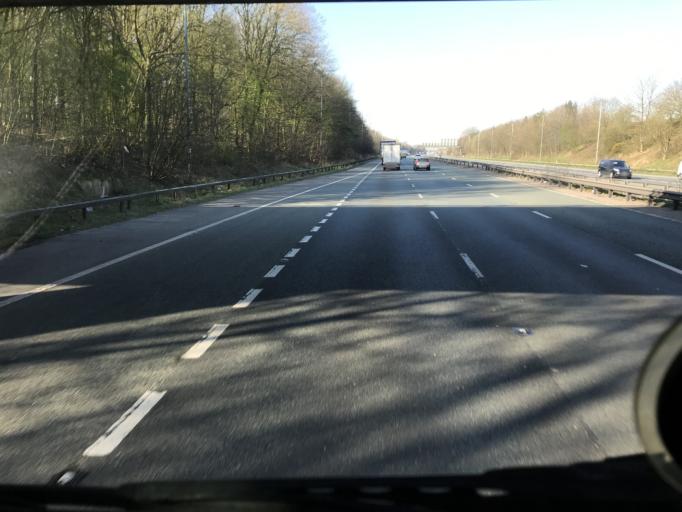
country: GB
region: England
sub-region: Warrington
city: Appleton Thorn
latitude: 53.3483
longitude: -2.5186
